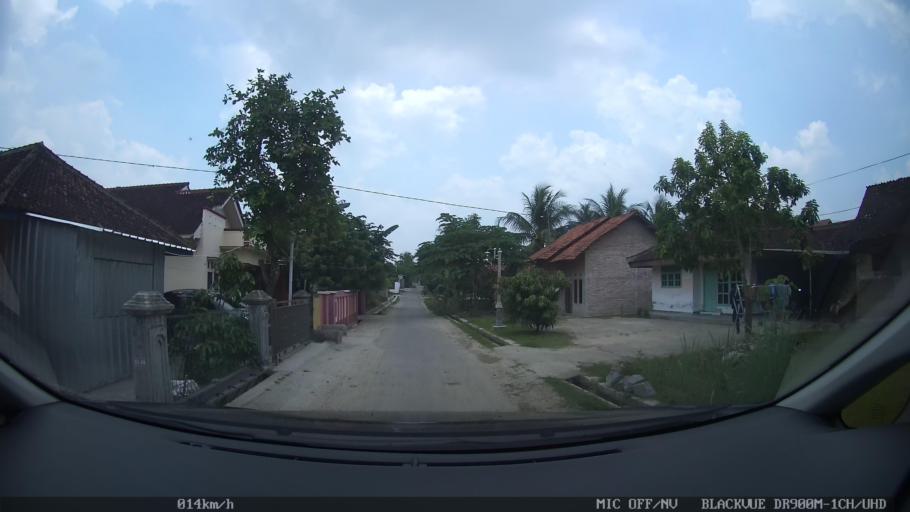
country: ID
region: Lampung
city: Pringsewu
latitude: -5.3456
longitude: 104.9785
